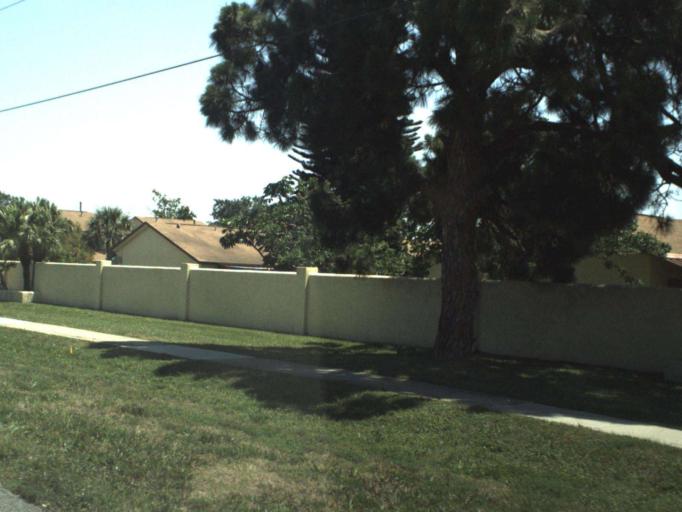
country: US
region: Florida
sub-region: Brevard County
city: Cocoa
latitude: 28.3860
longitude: -80.7028
